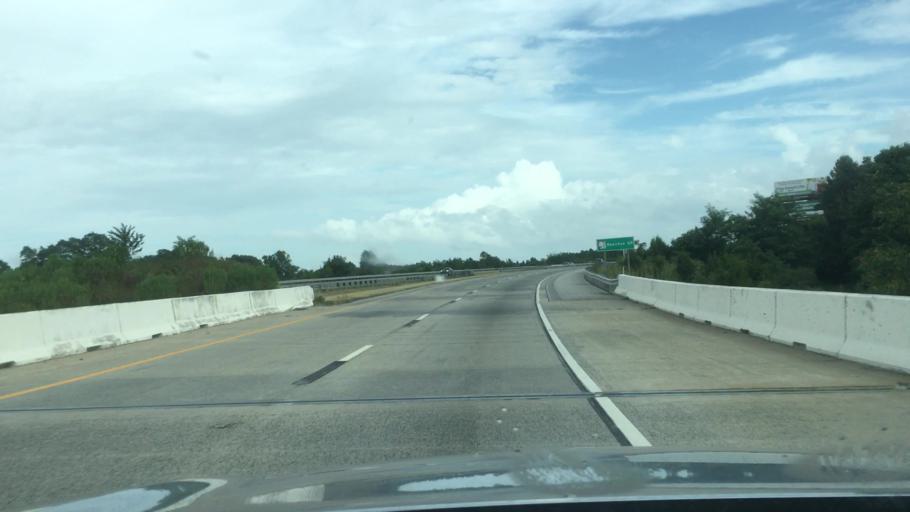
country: US
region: Delaware
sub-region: New Castle County
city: Middletown
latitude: 39.4415
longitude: -75.6638
